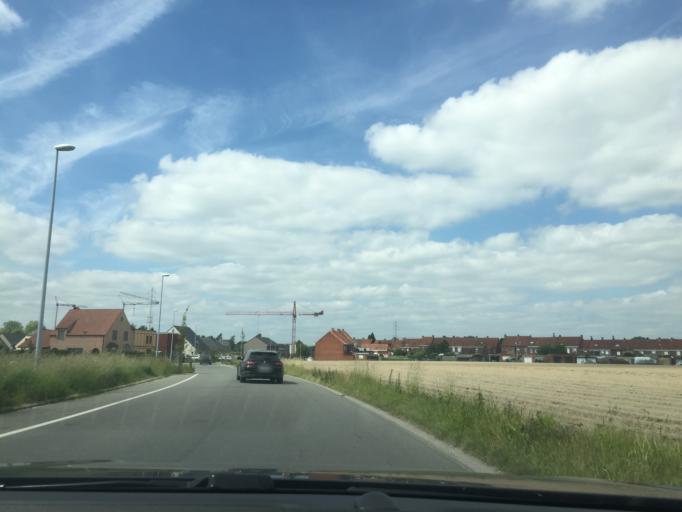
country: BE
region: Flanders
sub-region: Provincie West-Vlaanderen
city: Izegem
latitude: 50.9080
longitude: 3.2312
